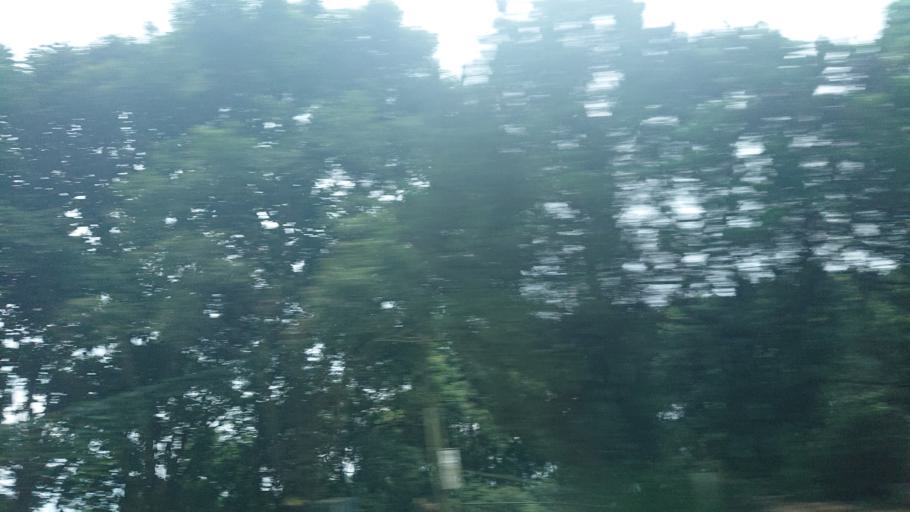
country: TW
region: Taiwan
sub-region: Chiayi
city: Jiayi Shi
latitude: 23.4708
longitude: 120.7085
